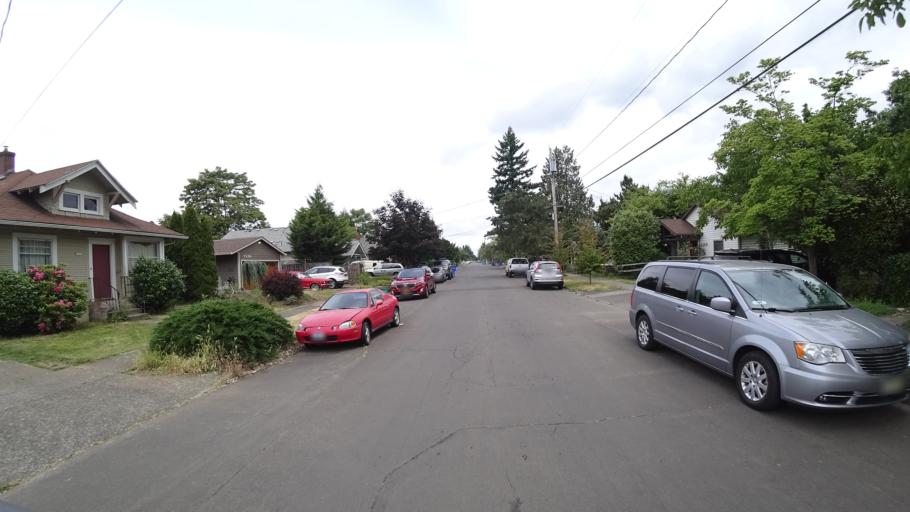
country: US
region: Oregon
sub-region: Multnomah County
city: Lents
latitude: 45.4711
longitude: -122.5780
